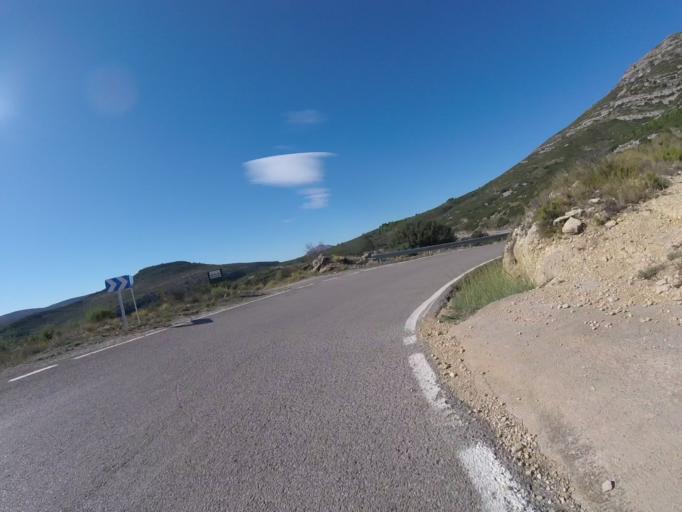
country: ES
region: Valencia
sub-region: Provincia de Castello
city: Albocasser
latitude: 40.3960
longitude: 0.0436
